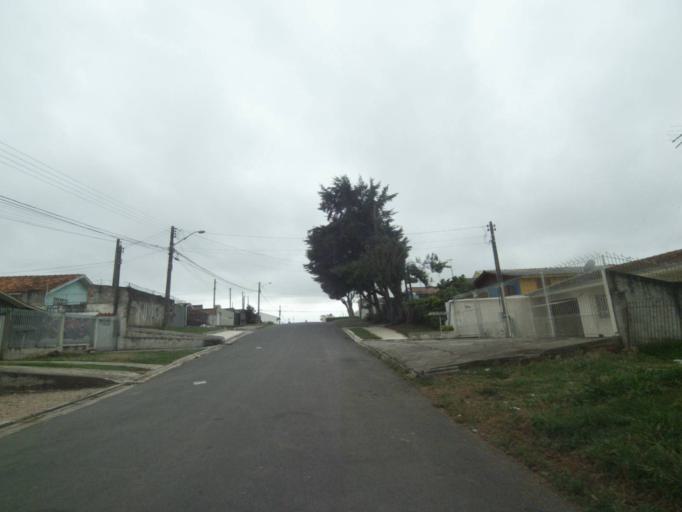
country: BR
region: Parana
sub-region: Sao Jose Dos Pinhais
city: Sao Jose dos Pinhais
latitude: -25.5466
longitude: -49.2816
